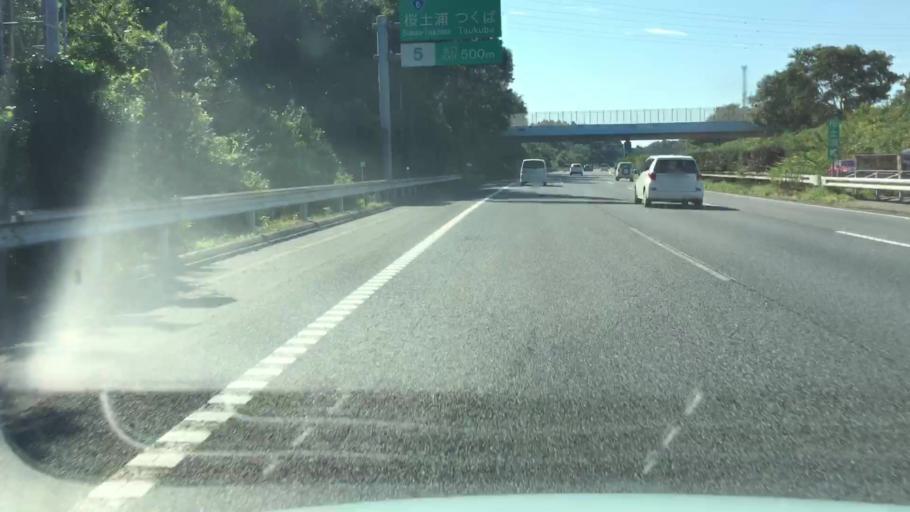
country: JP
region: Ibaraki
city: Naka
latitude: 36.0639
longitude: 140.1578
